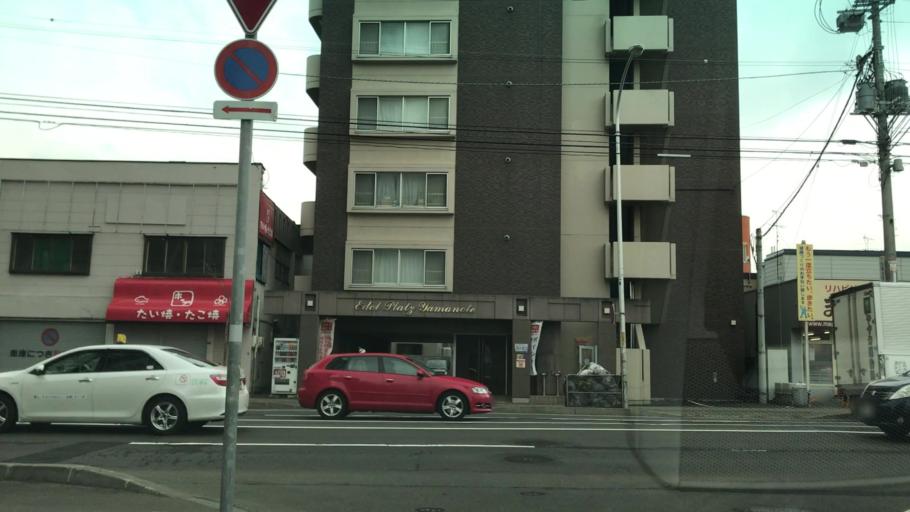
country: JP
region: Hokkaido
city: Sapporo
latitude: 43.0741
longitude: 141.2978
